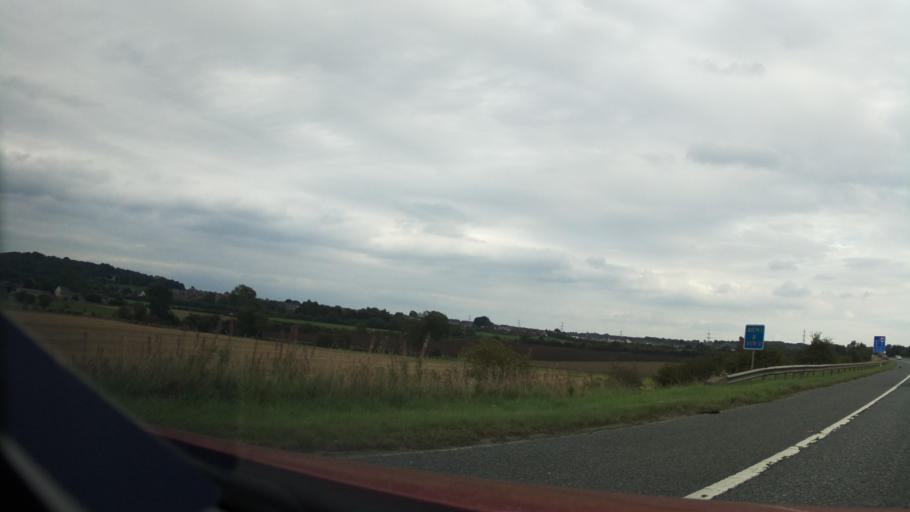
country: GB
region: England
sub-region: County Durham
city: West Cornforth
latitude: 54.7192
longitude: -1.5210
